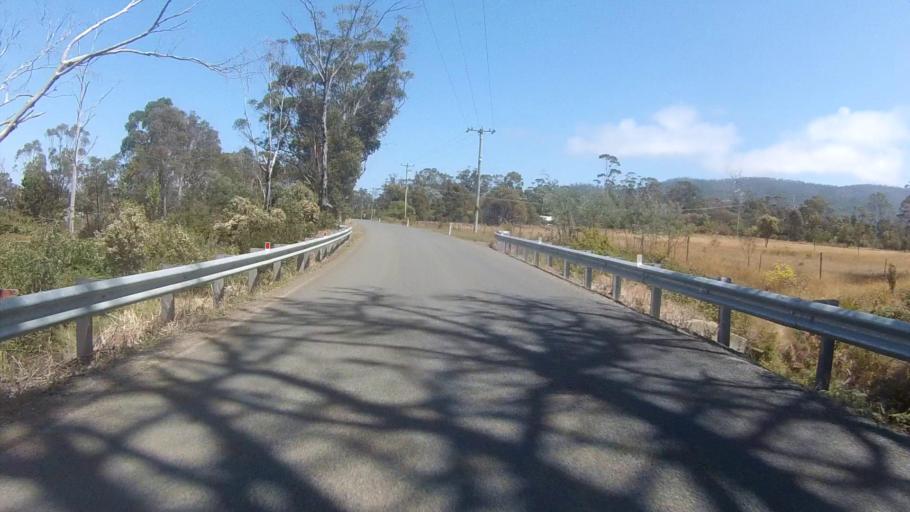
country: AU
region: Tasmania
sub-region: Sorell
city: Sorell
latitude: -42.8564
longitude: 147.8371
